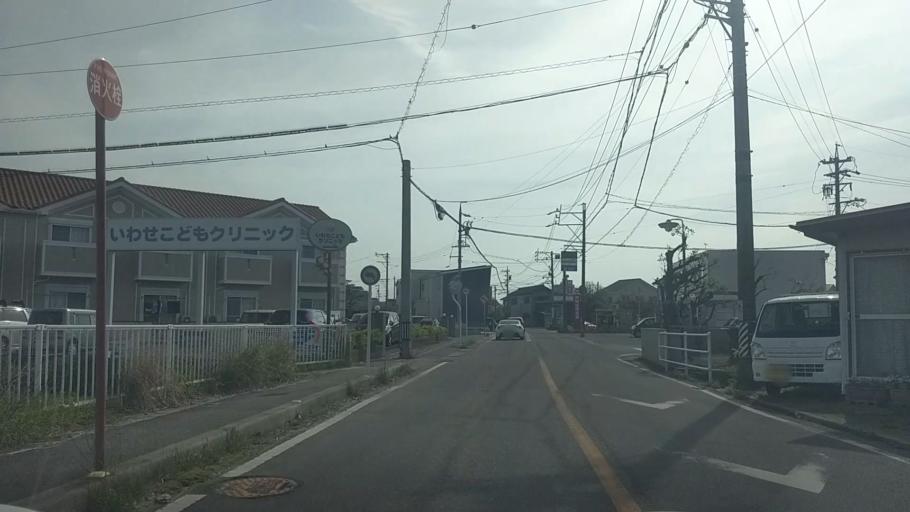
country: JP
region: Aichi
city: Okazaki
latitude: 34.9610
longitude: 137.1302
